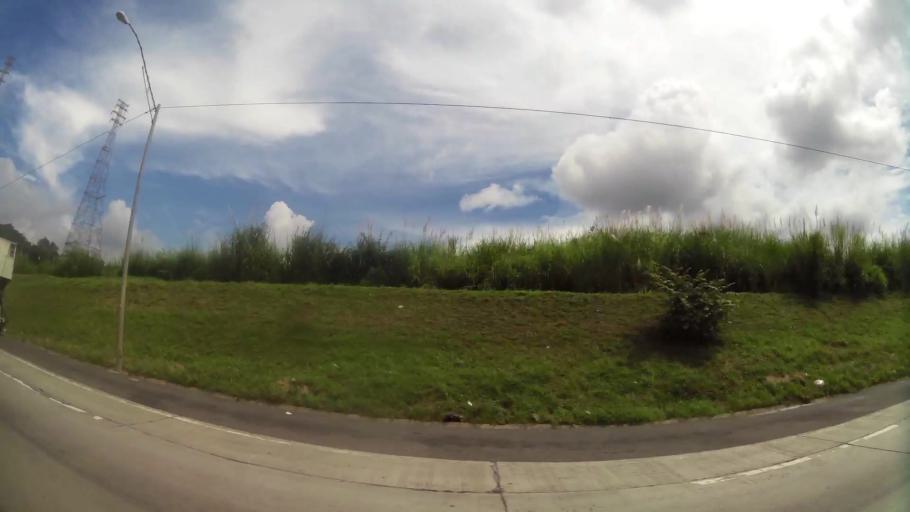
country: PA
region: Panama
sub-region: Distrito de Panama
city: Paraiso
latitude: 9.0232
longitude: -79.6392
